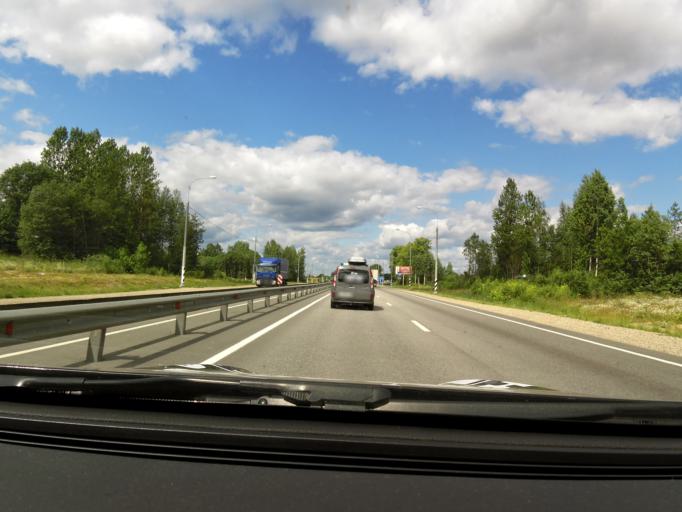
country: RU
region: Tverskaya
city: Torzhok
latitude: 57.0214
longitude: 35.0443
